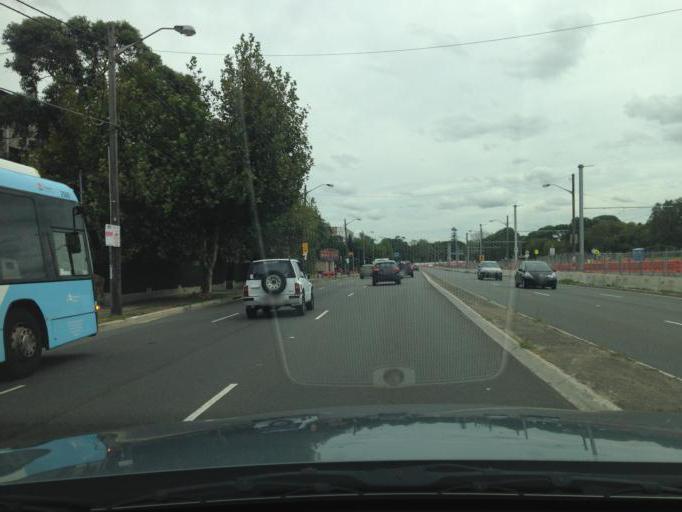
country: AU
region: New South Wales
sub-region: Randwick
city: Kensington
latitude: -33.9041
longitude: 151.2258
